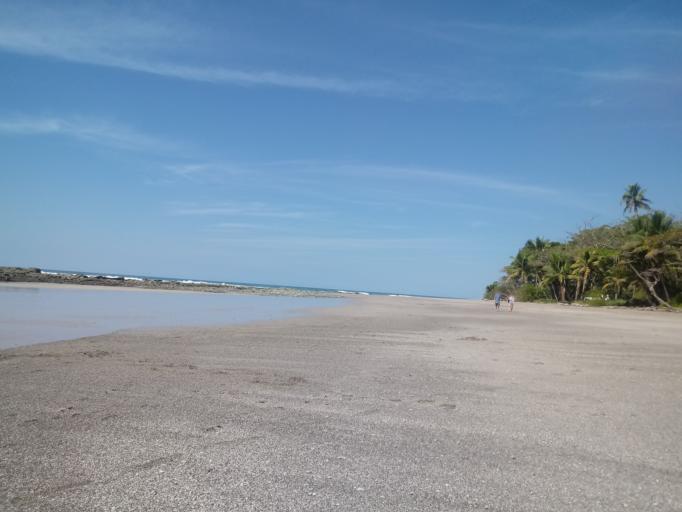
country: CR
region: Guanacaste
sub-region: Canton de Nandayure
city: Bejuco
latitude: 9.6686
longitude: -85.1951
